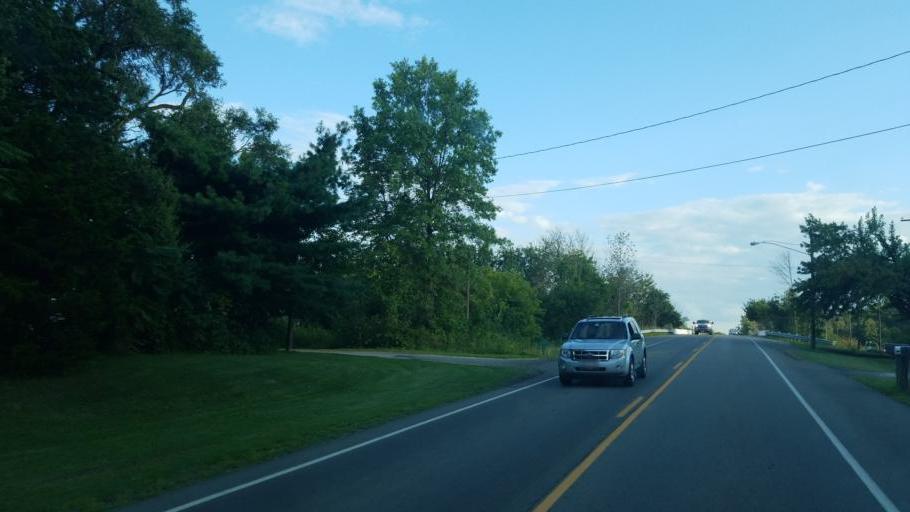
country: US
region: Ohio
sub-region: Huron County
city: Willard
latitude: 41.0597
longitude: -82.7165
